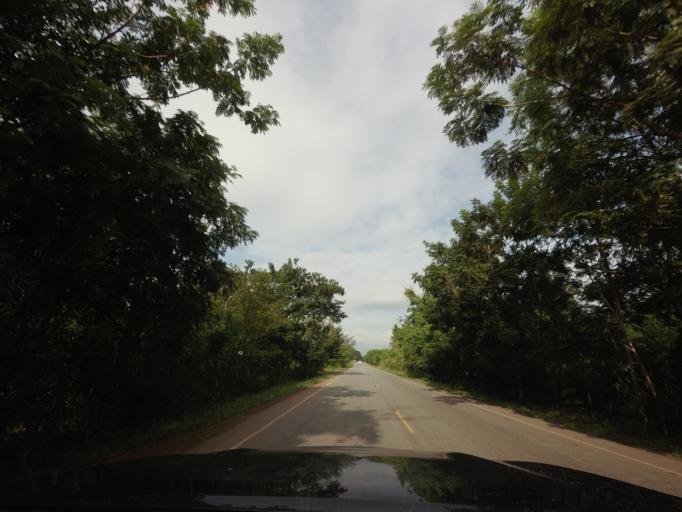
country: TH
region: Changwat Udon Thani
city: Nam Som
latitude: 17.8041
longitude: 102.3018
